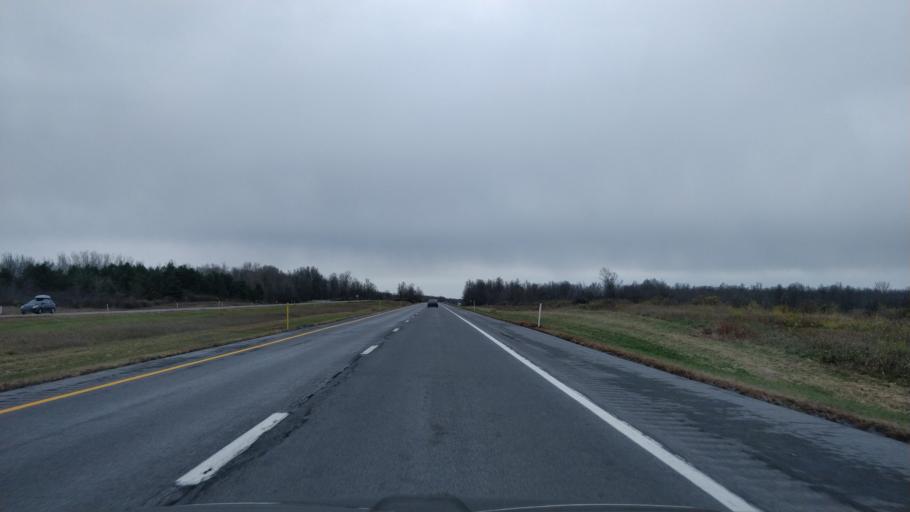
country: US
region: New York
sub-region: Jefferson County
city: Calcium
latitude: 44.0877
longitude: -75.9151
